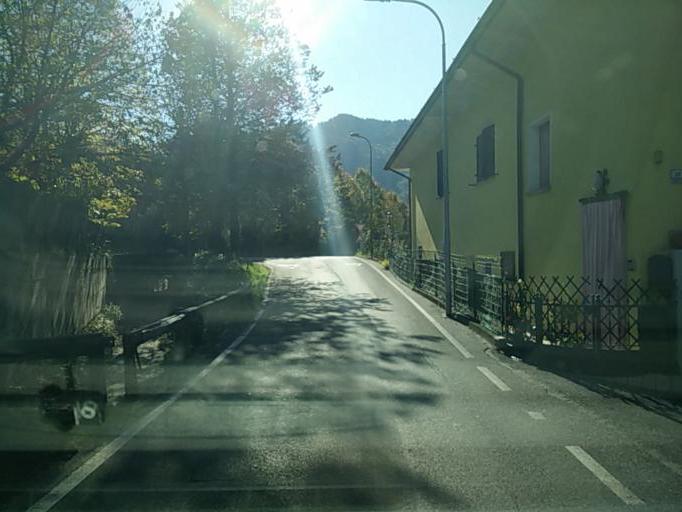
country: IT
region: Lombardy
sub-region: Provincia di Brescia
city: Idro
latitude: 45.7357
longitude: 10.4638
